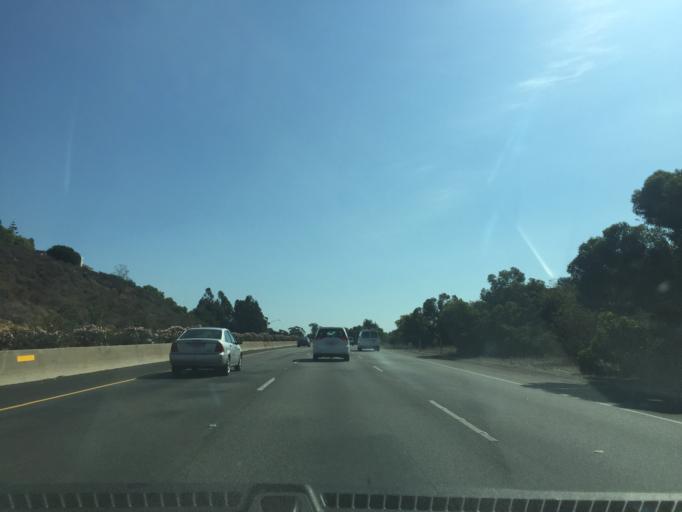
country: US
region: California
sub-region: Santa Barbara County
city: Goleta
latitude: 34.4418
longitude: -119.7749
